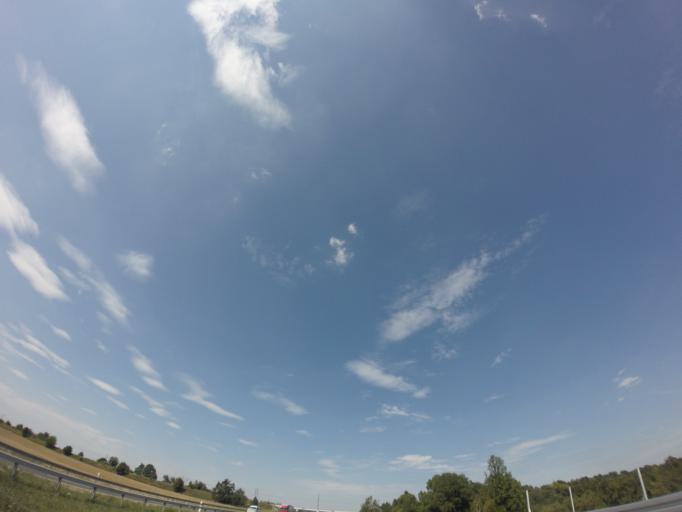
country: PL
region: Lower Silesian Voivodeship
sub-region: Legnica
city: Legnica
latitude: 51.2283
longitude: 16.1410
